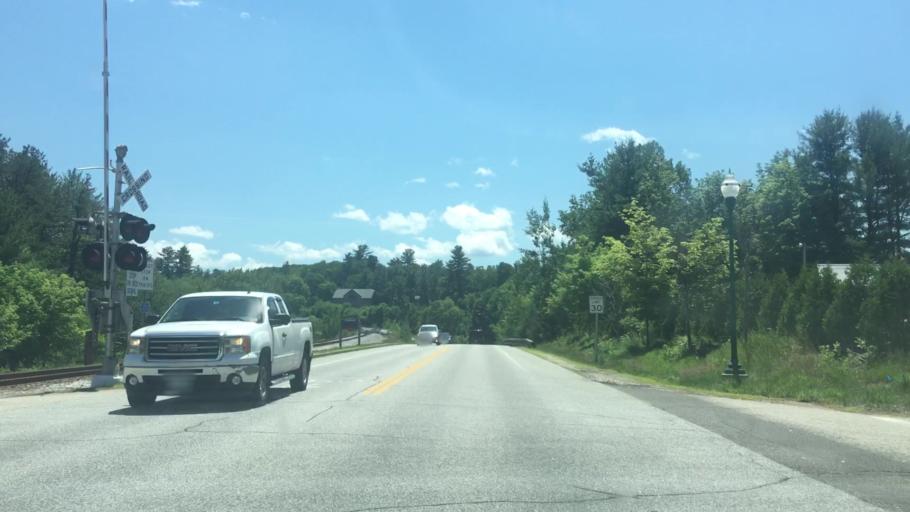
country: US
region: New Hampshire
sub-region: Carroll County
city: North Conway
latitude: 44.0471
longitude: -71.1229
